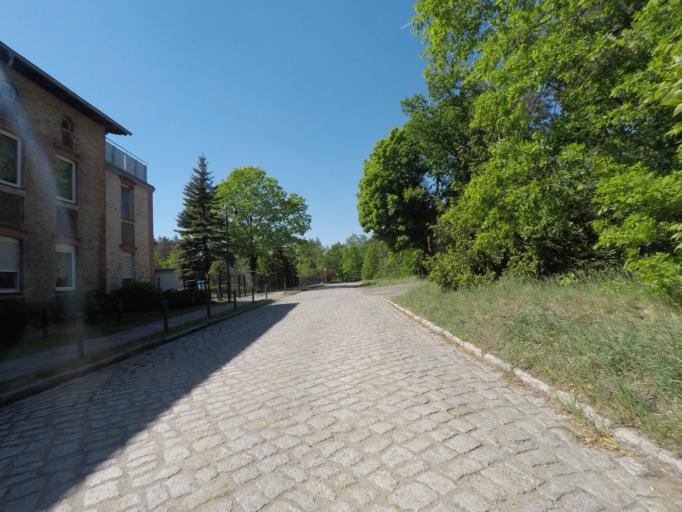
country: DE
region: Brandenburg
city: Eberswalde
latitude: 52.8124
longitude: 13.7737
